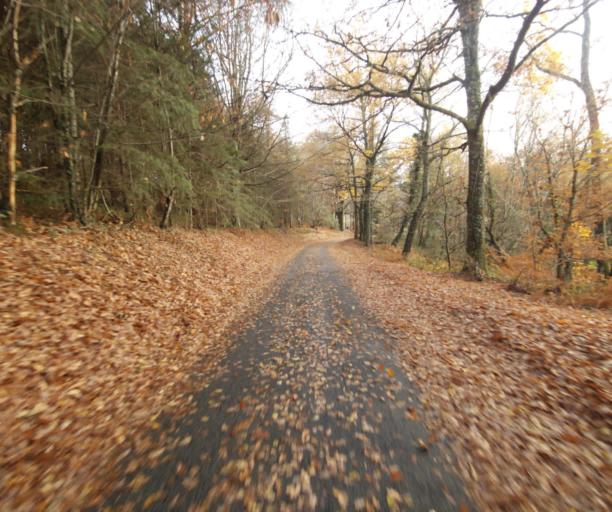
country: FR
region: Limousin
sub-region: Departement de la Correze
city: Cornil
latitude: 45.2000
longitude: 1.7021
